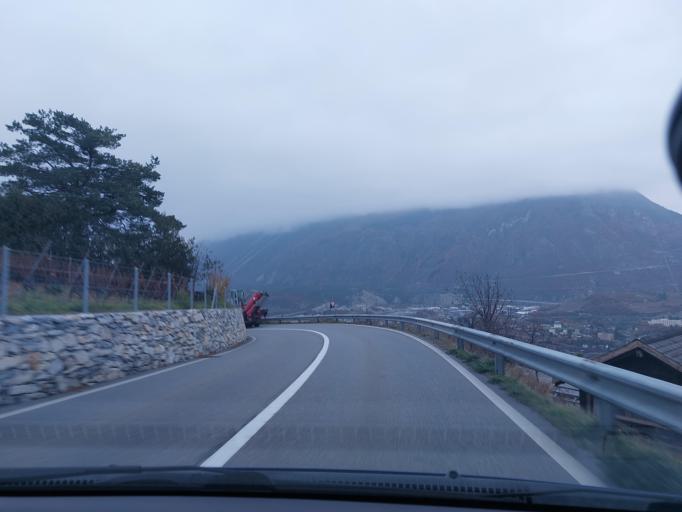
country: CH
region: Valais
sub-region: Sierre District
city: Veyras
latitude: 46.3019
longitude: 7.5296
